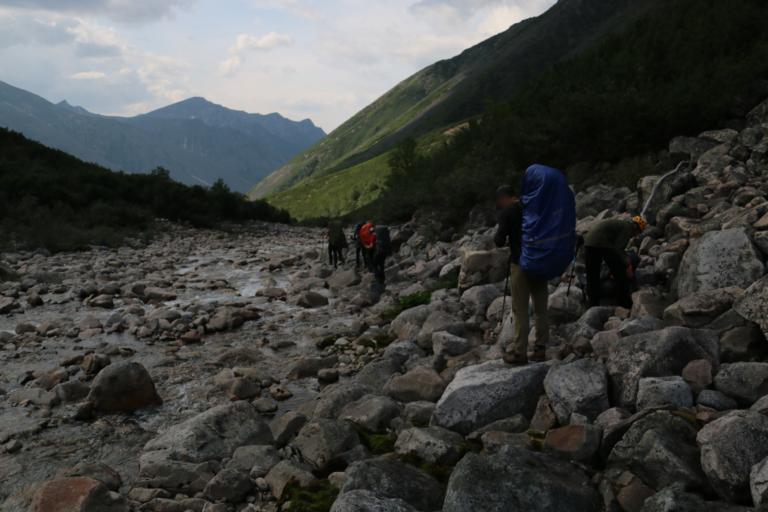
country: RU
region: Respublika Buryatiya
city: Novyy Uoyan
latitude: 56.3195
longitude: 111.2064
